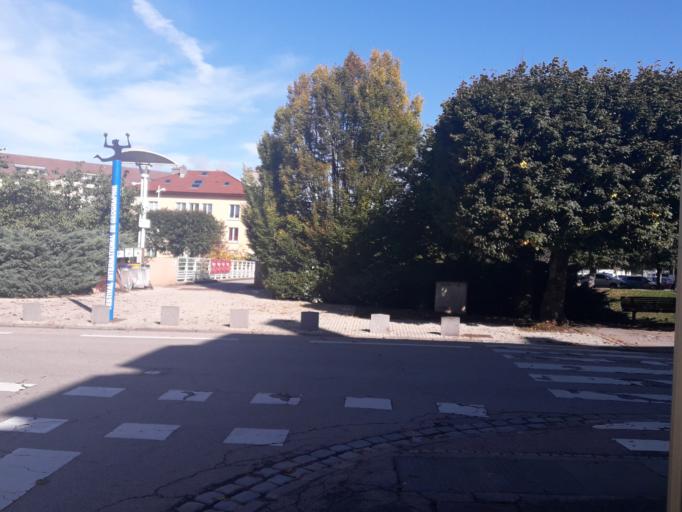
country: FR
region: Lorraine
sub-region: Departement des Vosges
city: Saint-Die-des-Vosges
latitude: 48.2843
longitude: 6.9531
